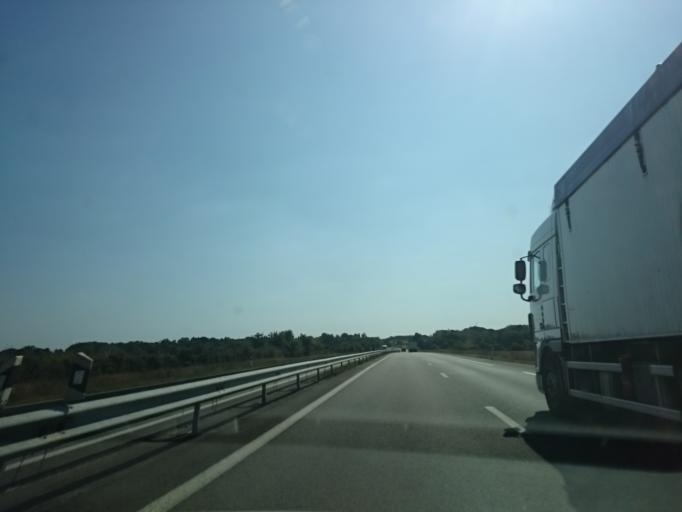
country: FR
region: Brittany
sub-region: Departement d'Ille-et-Vilaine
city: La Dominelais
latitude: 47.7612
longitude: -1.7119
